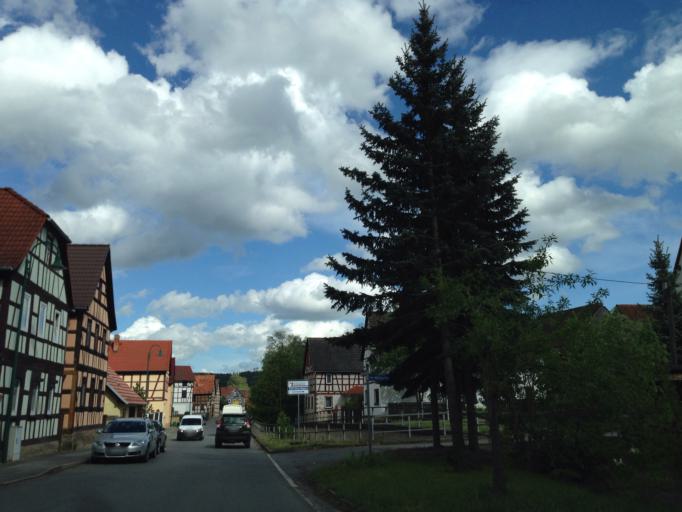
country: DE
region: Thuringia
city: Orlamunde
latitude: 50.7540
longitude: 11.5024
